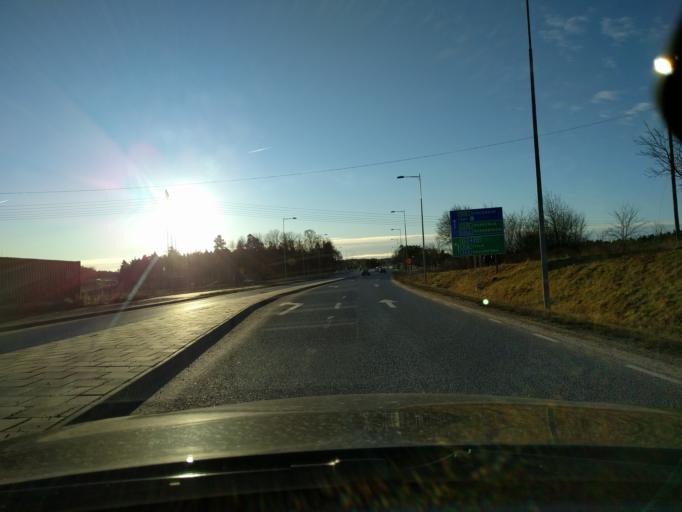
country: SE
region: Stockholm
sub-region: Taby Kommun
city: Taby
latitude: 59.4784
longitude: 18.0537
